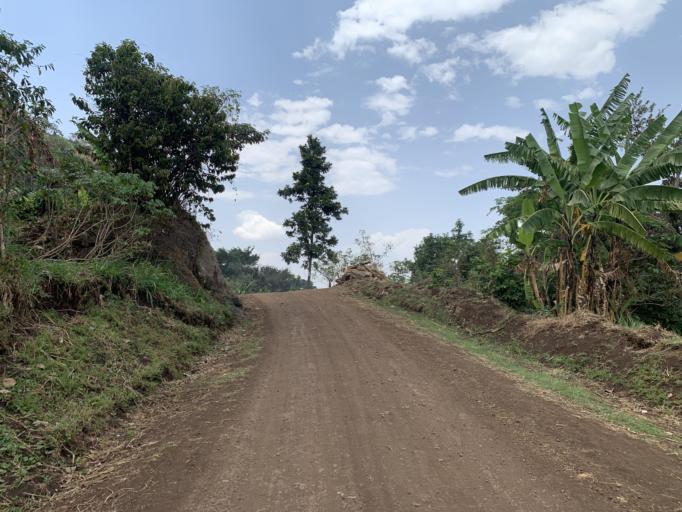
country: UG
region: Eastern Region
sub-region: Sironko District
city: Sironko
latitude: 1.2601
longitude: 34.3054
